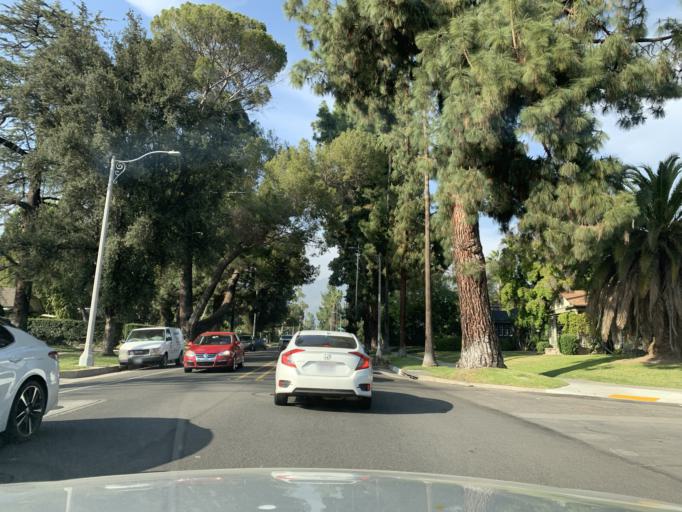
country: US
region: California
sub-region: Los Angeles County
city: Pasadena
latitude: 34.1602
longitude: -118.1215
